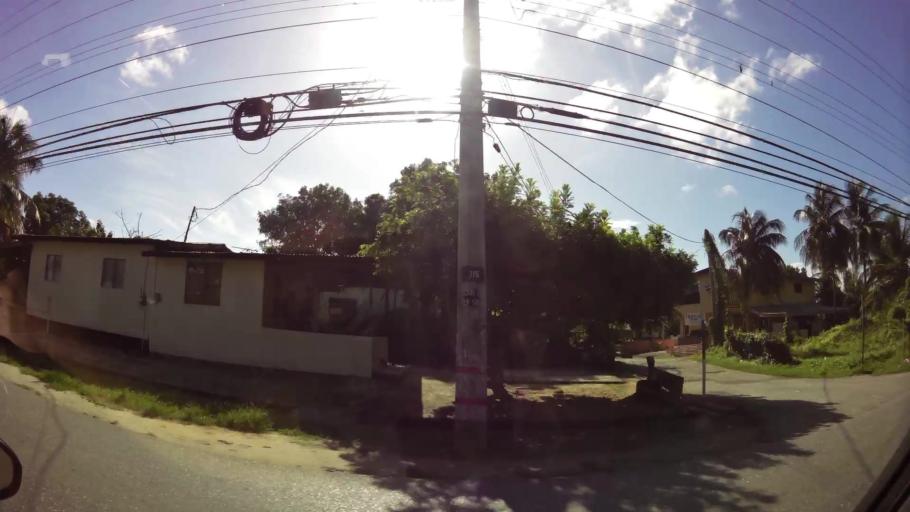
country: TT
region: Chaguanas
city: Chaguanas
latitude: 10.5284
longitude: -61.4059
